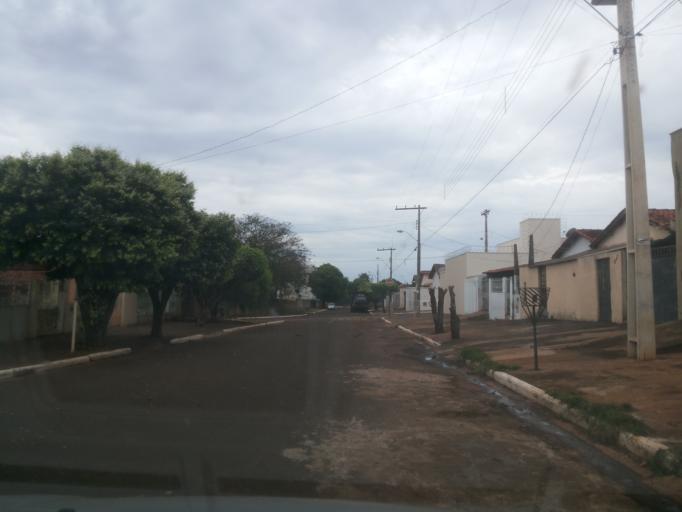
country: BR
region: Minas Gerais
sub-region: Ituiutaba
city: Ituiutaba
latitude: -18.9714
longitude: -49.4773
